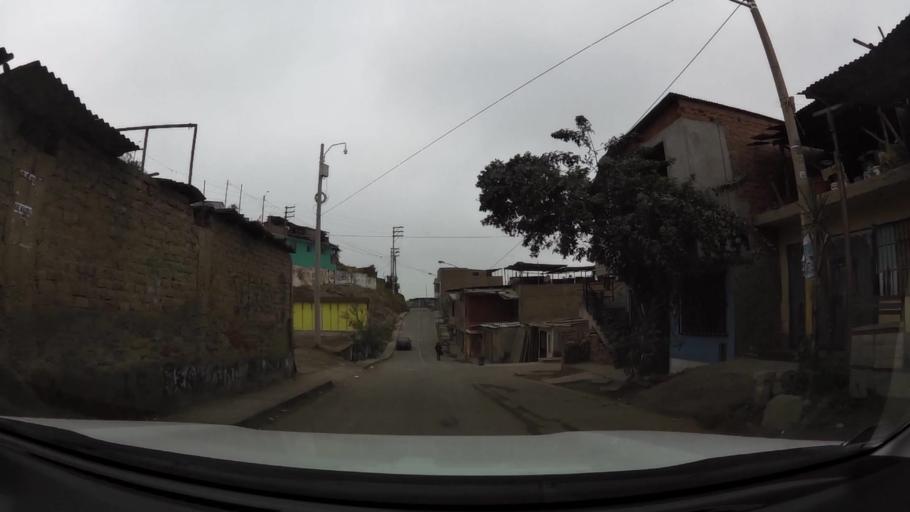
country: PE
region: Lima
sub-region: Lima
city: Surco
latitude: -12.1841
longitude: -76.9541
